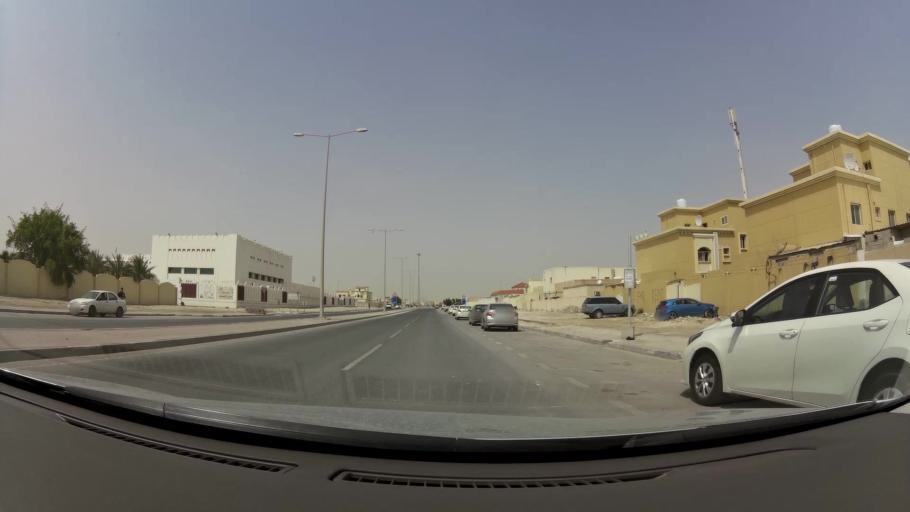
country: QA
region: Baladiyat ar Rayyan
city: Ar Rayyan
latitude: 25.2378
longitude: 51.4204
